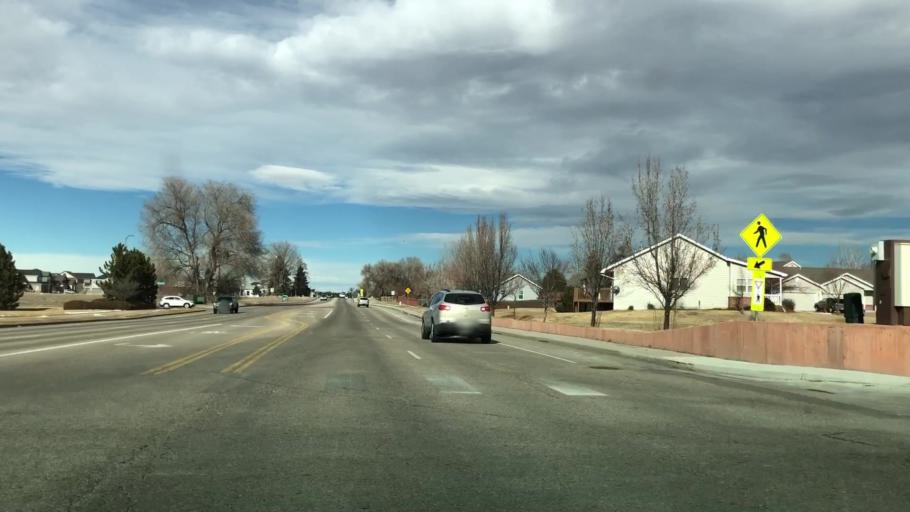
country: US
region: Colorado
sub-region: Weld County
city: Windsor
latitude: 40.4810
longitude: -104.9264
